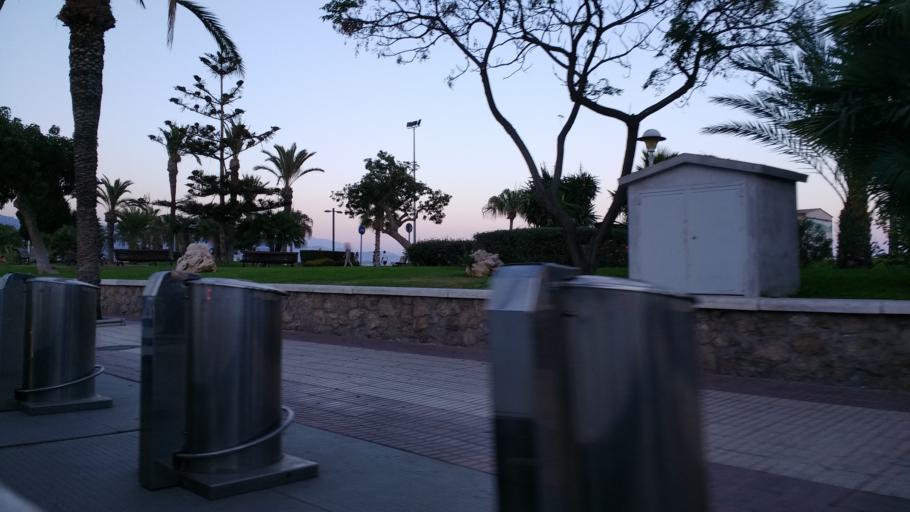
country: ES
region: Andalusia
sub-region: Provincia de Malaga
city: Velez-Malaga
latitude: 36.7412
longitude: -4.0902
